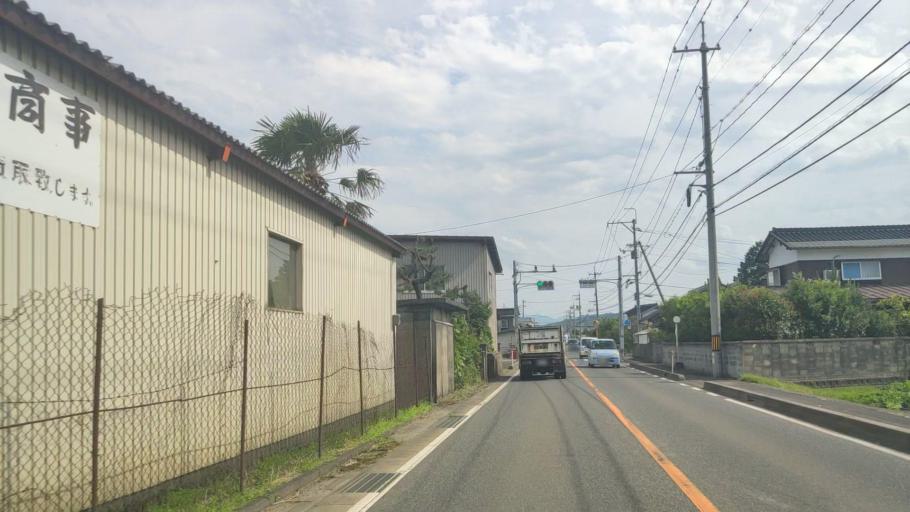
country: JP
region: Tottori
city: Tottori
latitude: 35.4673
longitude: 134.2038
